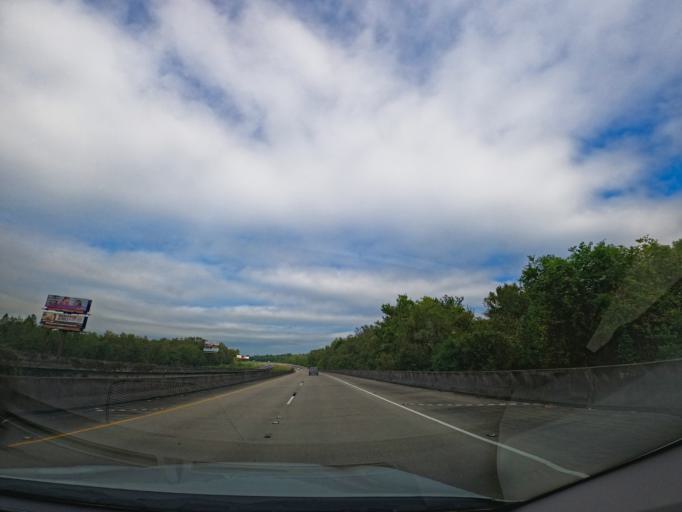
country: US
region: Louisiana
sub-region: Saint Mary Parish
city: Amelia
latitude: 29.6923
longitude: -91.1487
